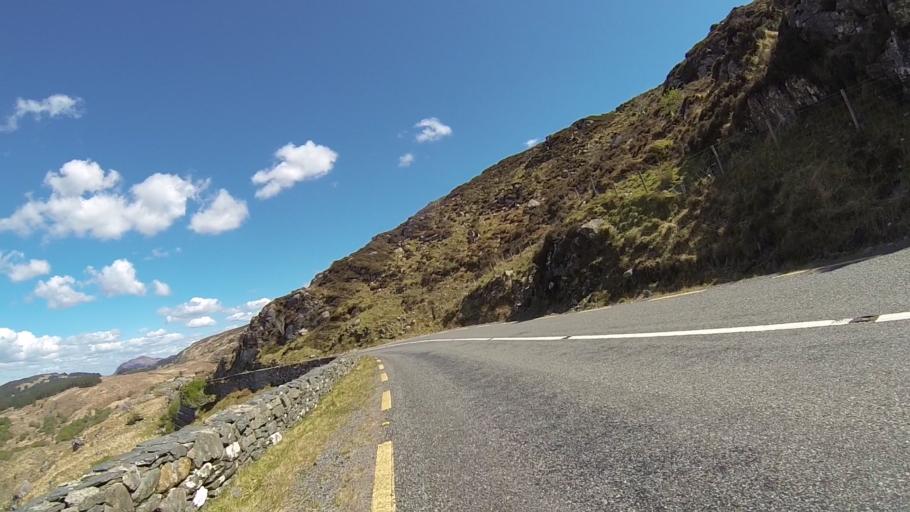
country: IE
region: Munster
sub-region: Ciarrai
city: Kenmare
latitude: 51.9449
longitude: -9.6433
